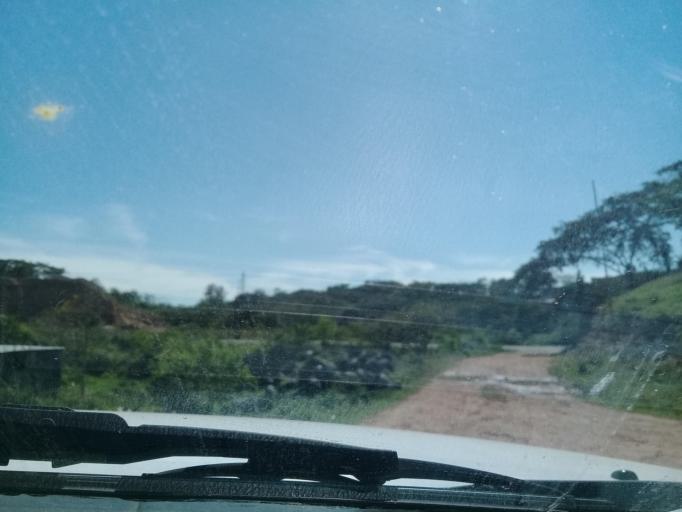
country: MX
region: Veracruz
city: El Castillo
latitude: 19.5490
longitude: -96.8493
